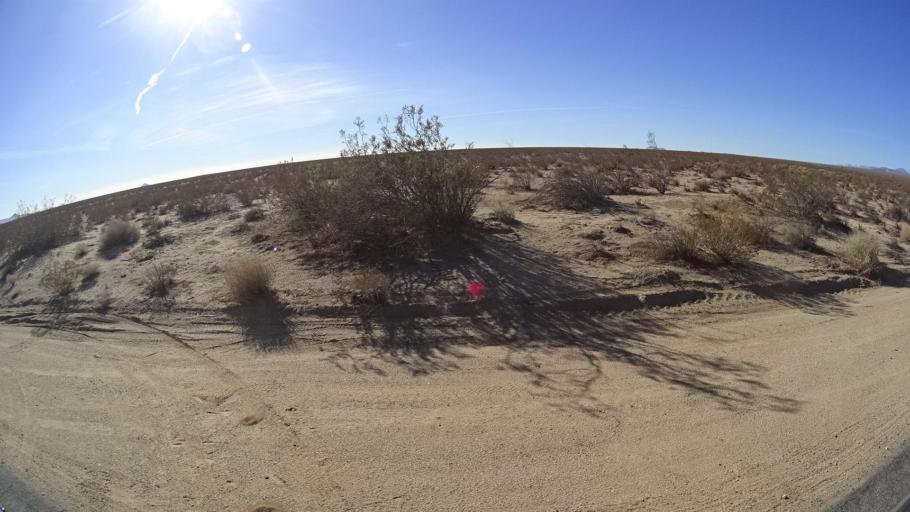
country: US
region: California
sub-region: Kern County
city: California City
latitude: 35.1985
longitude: -118.0555
